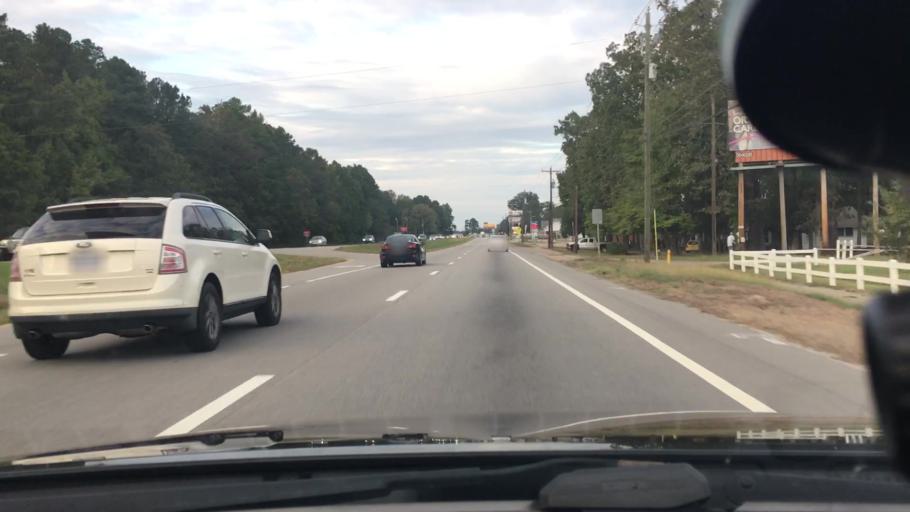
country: US
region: North Carolina
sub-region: Lee County
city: Sanford
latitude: 35.4242
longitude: -79.2249
